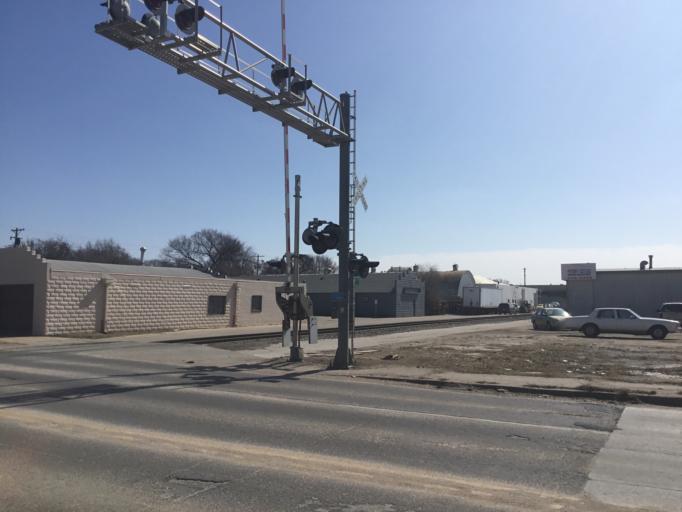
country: US
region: Kansas
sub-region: Sedgwick County
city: Wichita
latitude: 37.6644
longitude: -97.3292
